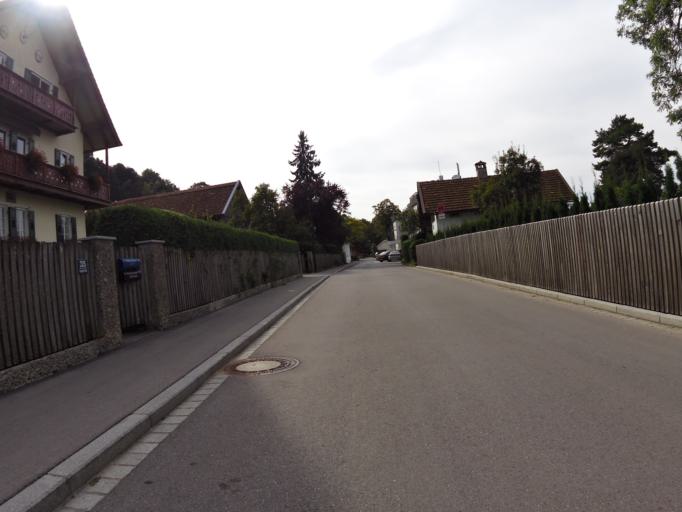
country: DE
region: Bavaria
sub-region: Upper Bavaria
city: Berg
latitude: 47.9563
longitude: 11.3443
